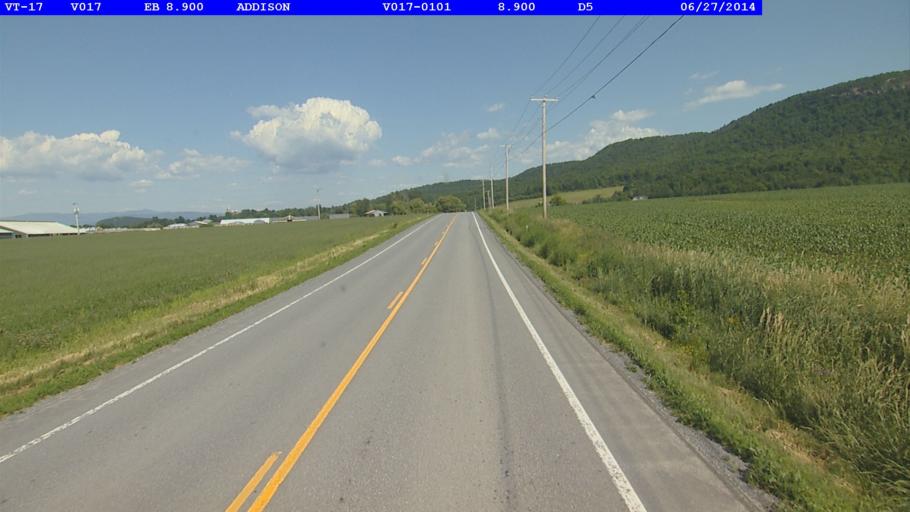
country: US
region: Vermont
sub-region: Addison County
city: Vergennes
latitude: 44.0863
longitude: -73.2926
